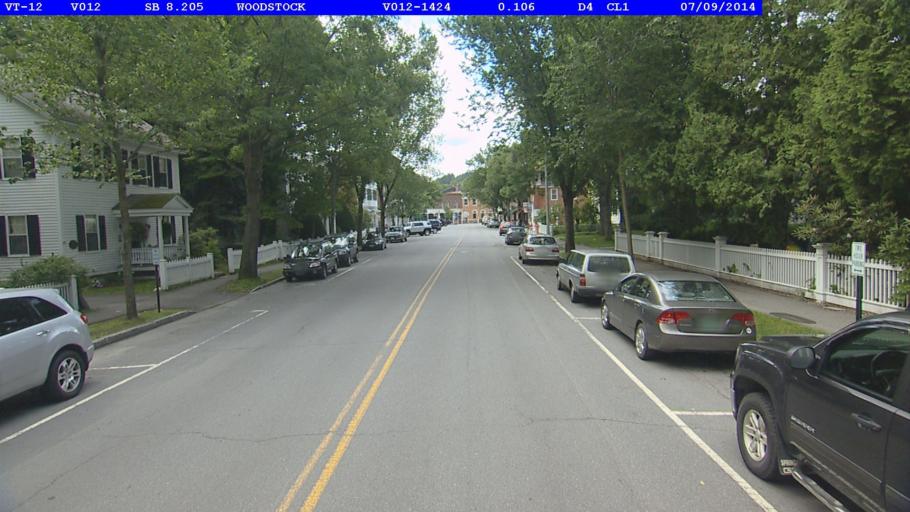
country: US
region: Vermont
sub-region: Windsor County
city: Woodstock
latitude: 43.6266
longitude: -72.5184
